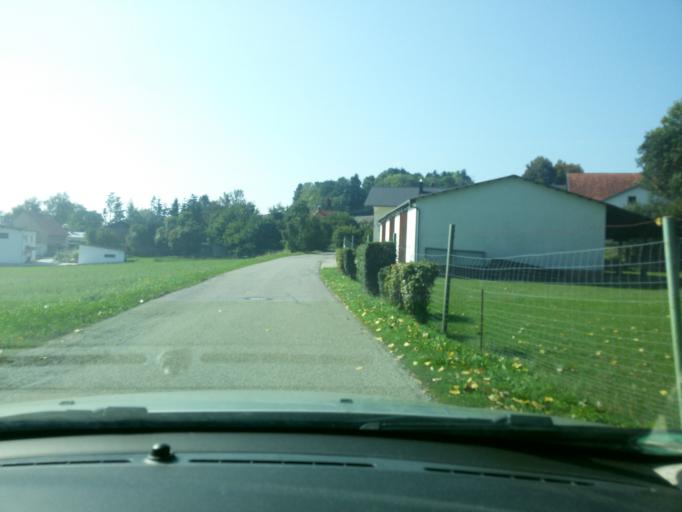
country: DE
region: Bavaria
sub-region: Swabia
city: Hiltenfingen
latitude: 48.1872
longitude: 10.6911
